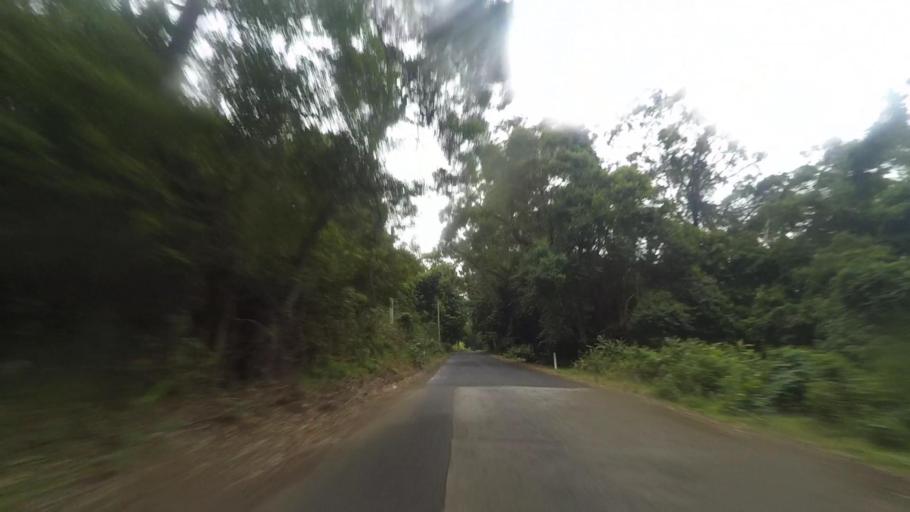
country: AU
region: New South Wales
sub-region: Wollongong
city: Cordeaux Heights
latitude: -34.4266
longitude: 150.8104
